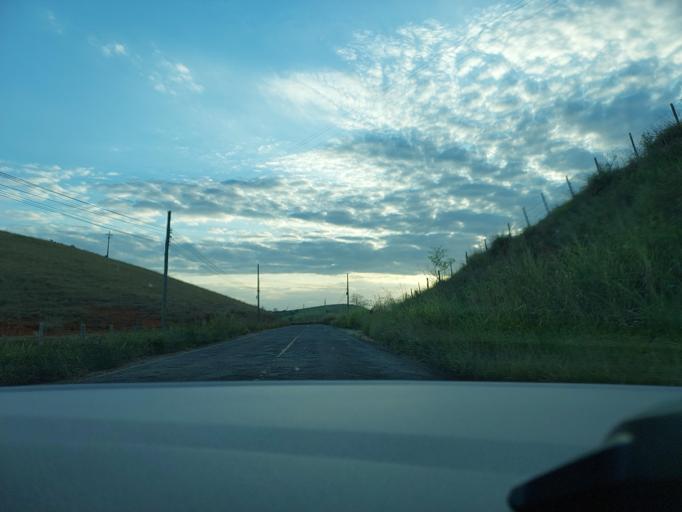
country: BR
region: Rio de Janeiro
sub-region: Natividade
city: Natividade
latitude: -21.1913
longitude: -42.1099
